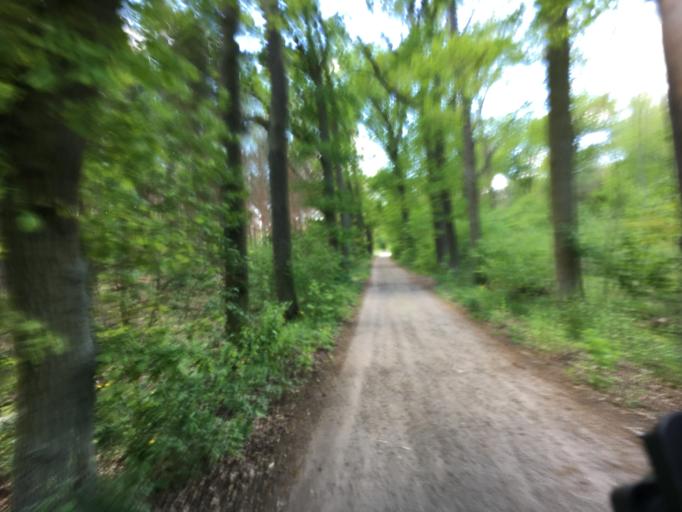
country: DE
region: Brandenburg
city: Trebbin
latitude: 52.1596
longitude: 13.1973
